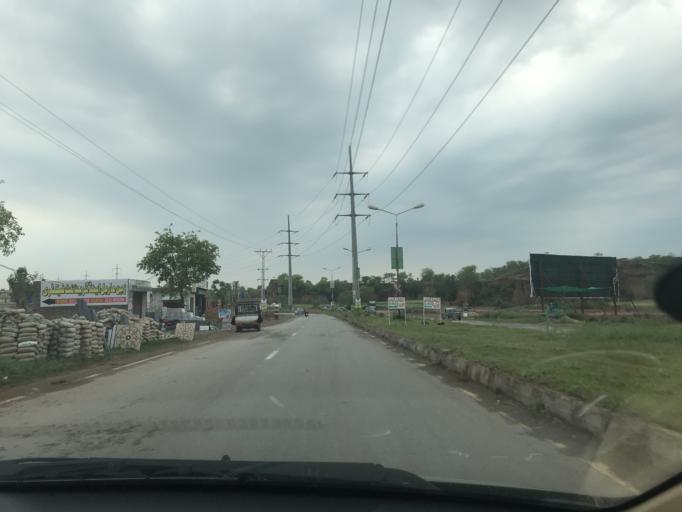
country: PK
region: Islamabad
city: Islamabad
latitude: 33.6884
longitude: 73.1705
